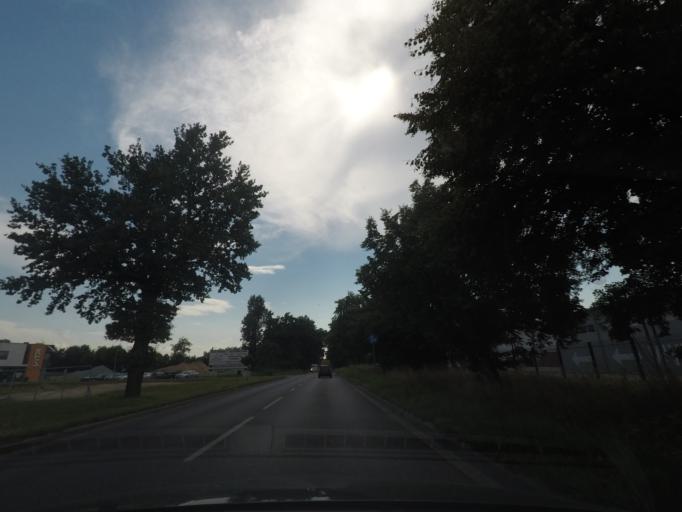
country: PL
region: Lesser Poland Voivodeship
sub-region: Powiat oswiecimski
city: Przecieszyn
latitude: 49.9899
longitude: 19.1641
